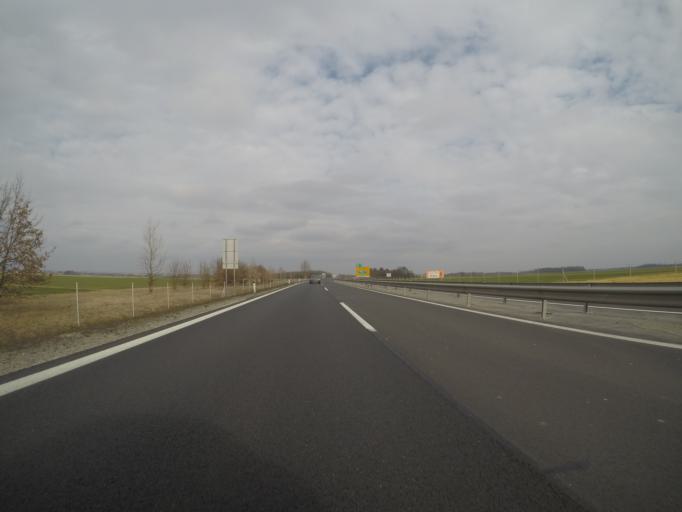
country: SI
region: Murska Sobota
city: Krog
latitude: 46.6302
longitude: 16.1443
